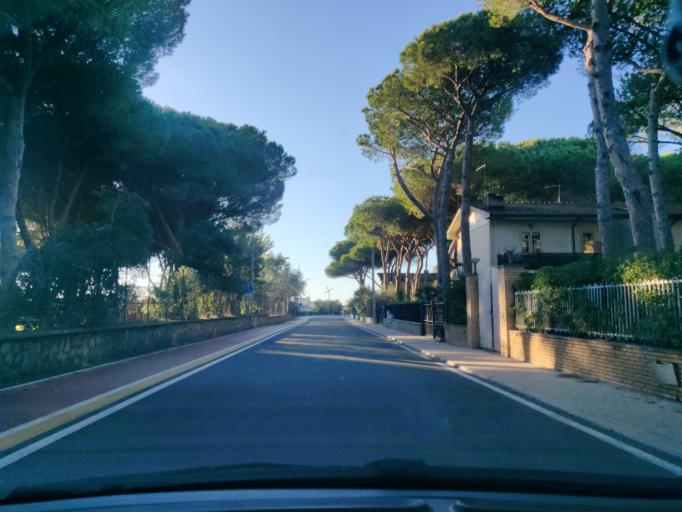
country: IT
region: Latium
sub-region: Provincia di Viterbo
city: Tarquinia
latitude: 42.2165
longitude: 11.7104
